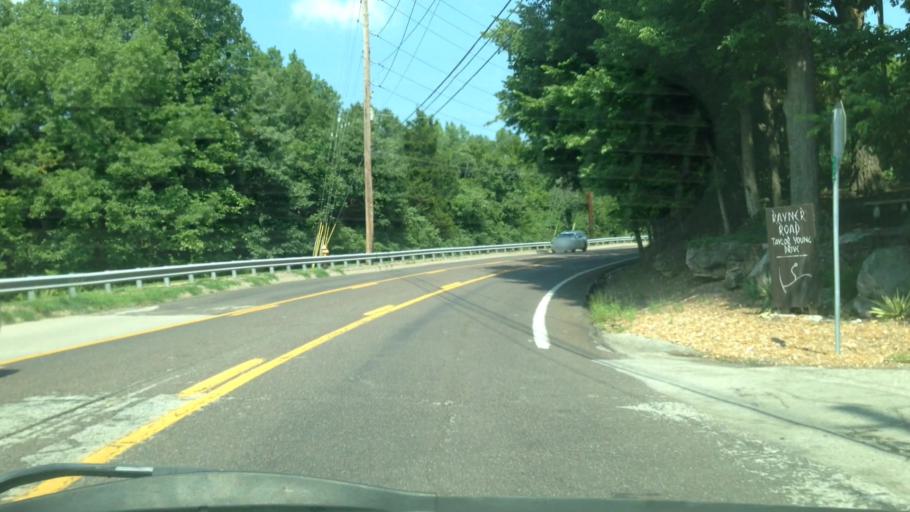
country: US
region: Missouri
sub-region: Saint Louis County
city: Des Peres
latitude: 38.5863
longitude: -90.4450
